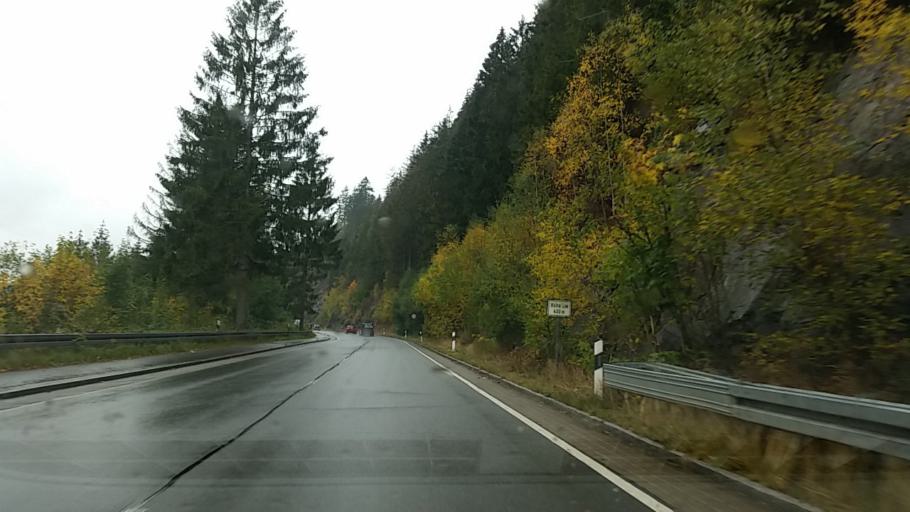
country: DE
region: Lower Saxony
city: Schulenberg im Oberharz
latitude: 51.8556
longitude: 10.4591
